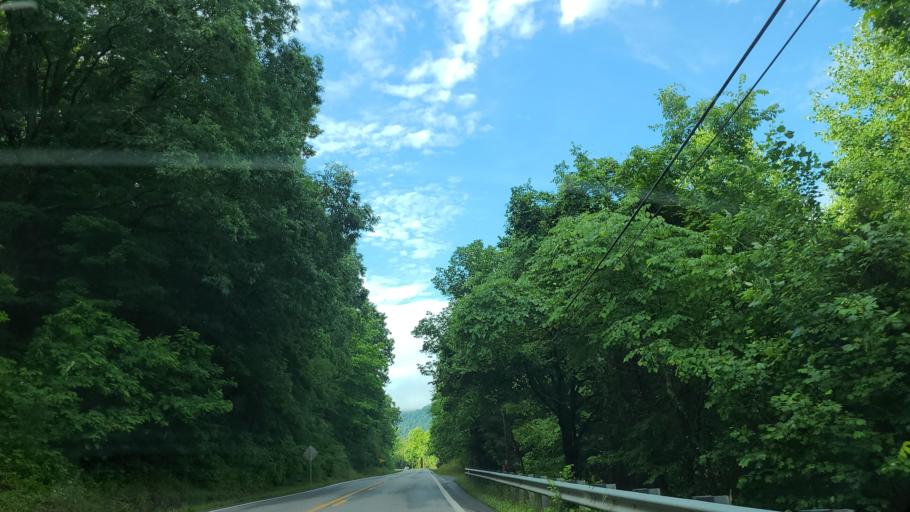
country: US
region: Kentucky
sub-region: Whitley County
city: Williamsburg
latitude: 36.7331
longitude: -84.1297
